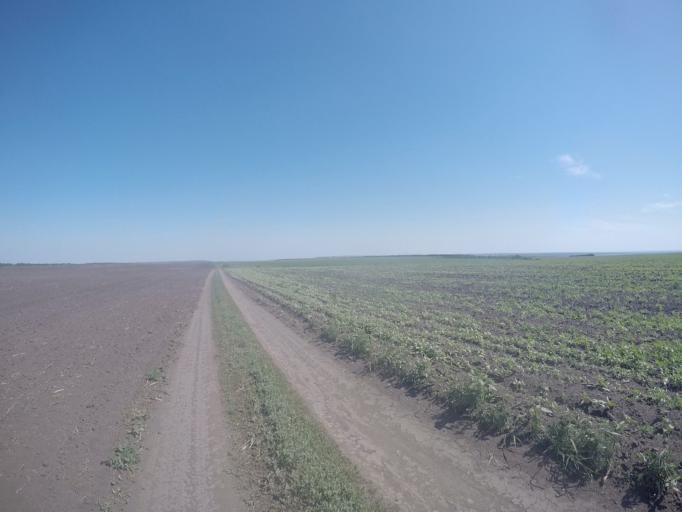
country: RU
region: Saratov
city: Krasnyy Oktyabr'
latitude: 51.3051
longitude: 45.5950
